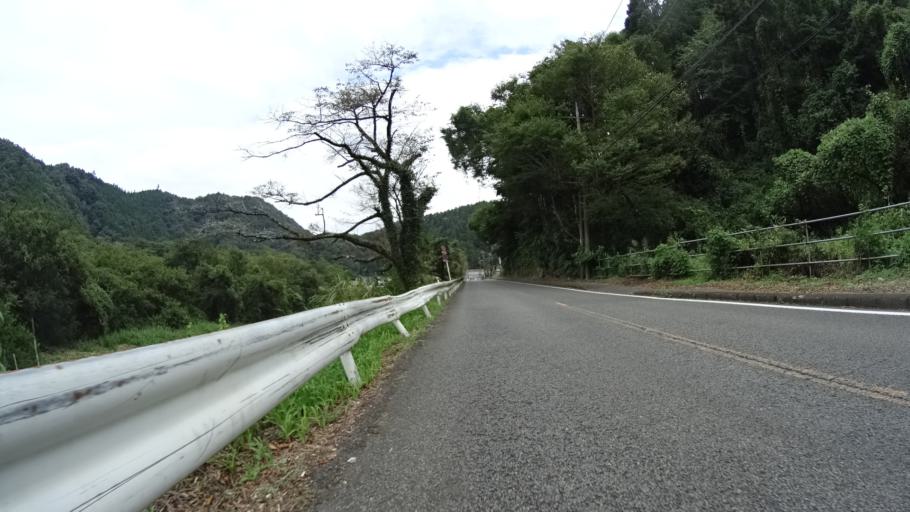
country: JP
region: Kanagawa
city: Zama
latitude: 35.5365
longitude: 139.2783
